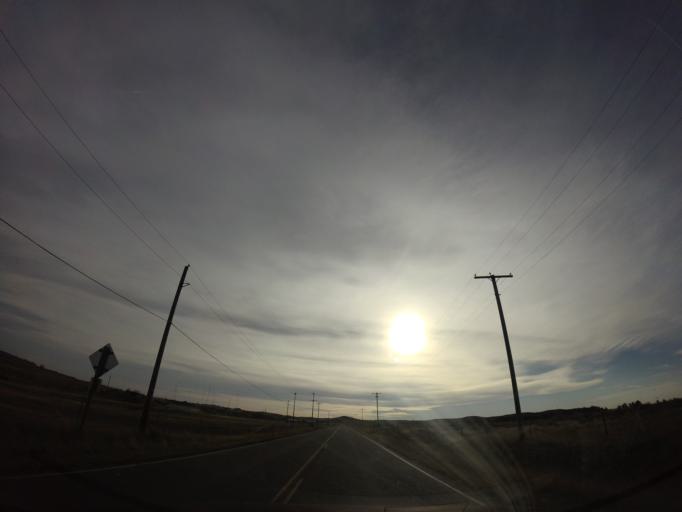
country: US
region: Montana
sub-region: Yellowstone County
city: Billings
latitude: 45.7848
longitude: -108.4593
